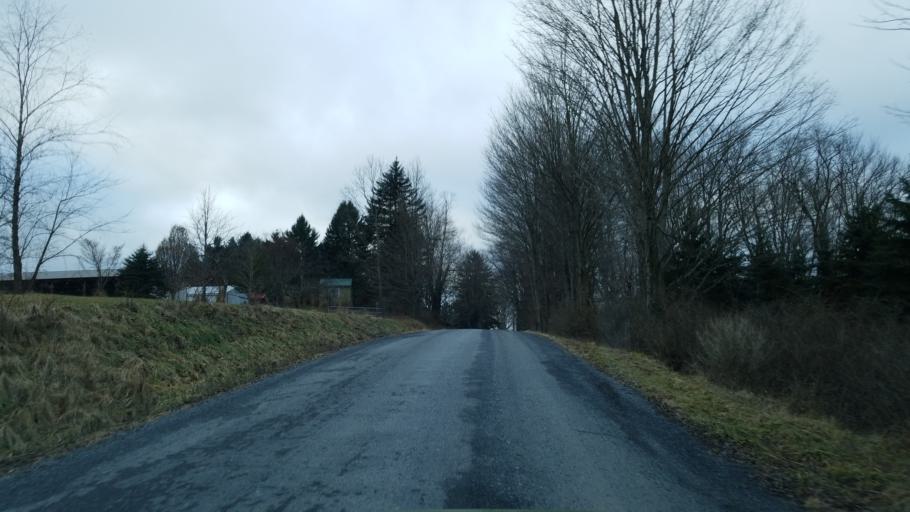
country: US
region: Pennsylvania
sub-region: Jefferson County
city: Falls Creek
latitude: 41.1808
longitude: -78.8011
